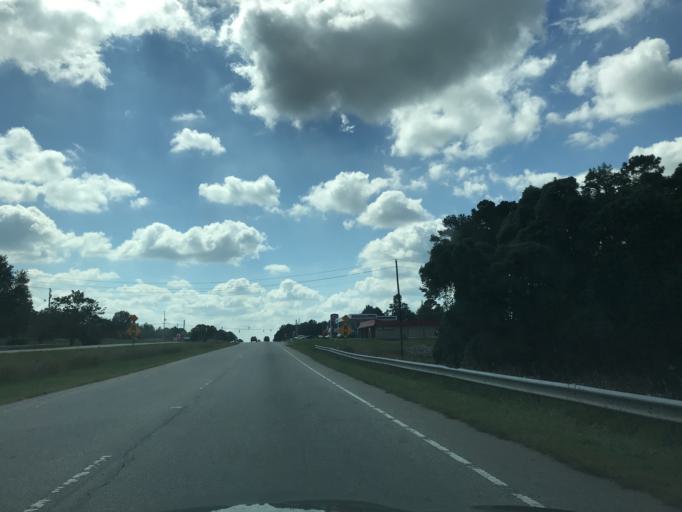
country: US
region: North Carolina
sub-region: Franklin County
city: Franklinton
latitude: 36.0997
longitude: -78.4676
